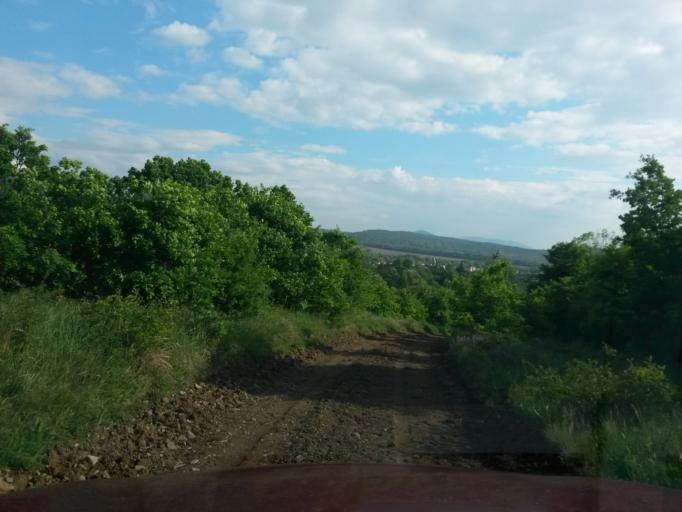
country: SK
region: Kosicky
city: Secovce
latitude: 48.7420
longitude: 21.4687
